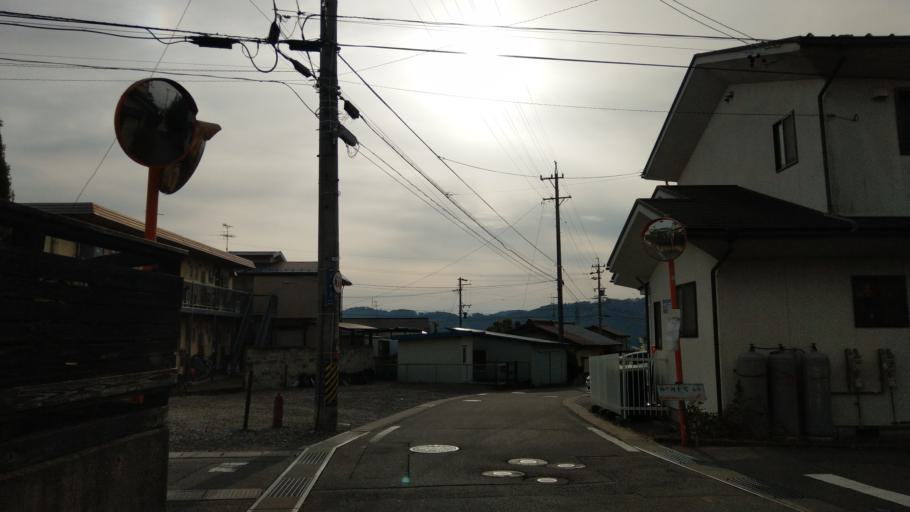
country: JP
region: Nagano
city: Komoro
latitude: 36.3141
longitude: 138.4367
